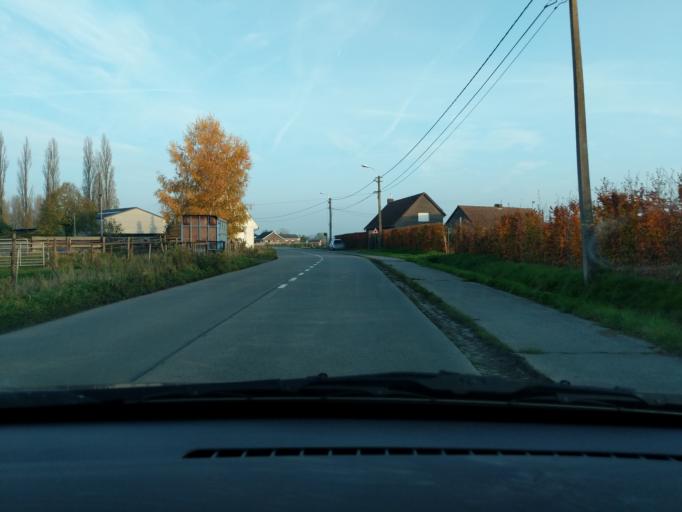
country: BE
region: Flanders
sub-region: Provincie Oost-Vlaanderen
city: Aalter
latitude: 51.0440
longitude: 3.4831
